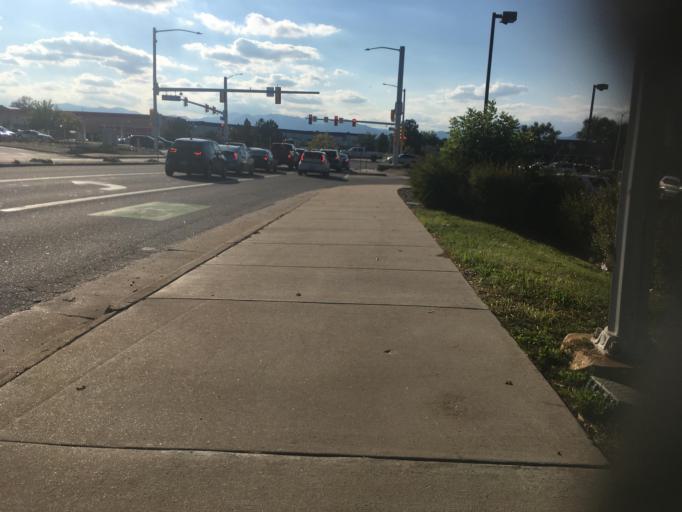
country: US
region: Colorado
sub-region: Broomfield County
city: Broomfield
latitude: 39.9222
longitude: -105.0898
